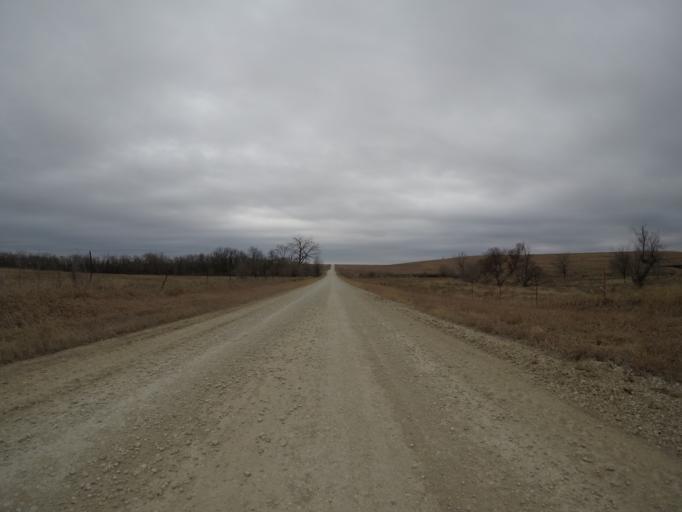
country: US
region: Kansas
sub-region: Wabaunsee County
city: Alma
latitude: 38.7948
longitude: -96.1500
